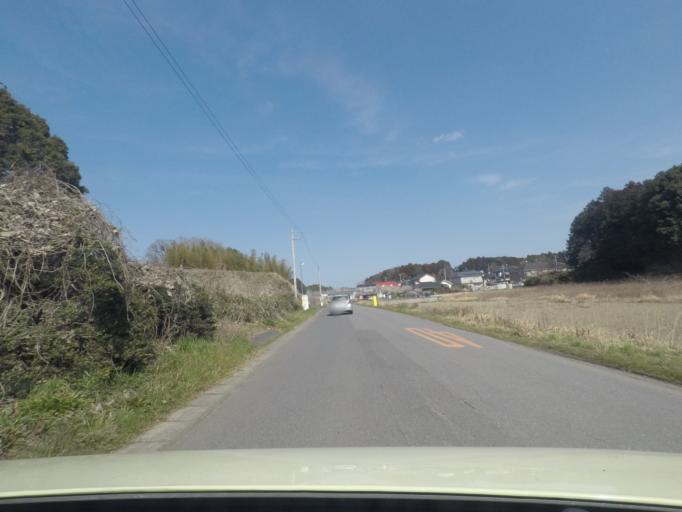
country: JP
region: Ibaraki
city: Ishioka
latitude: 36.1723
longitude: 140.3615
